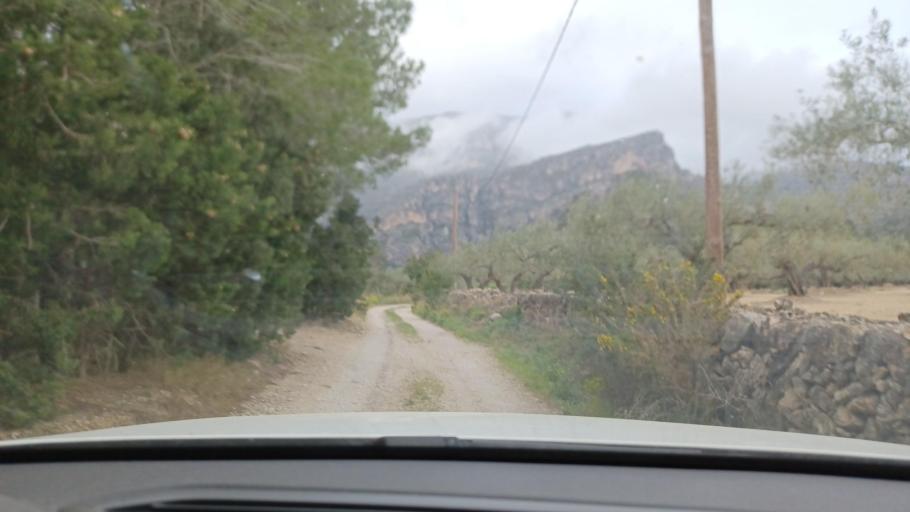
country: ES
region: Catalonia
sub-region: Provincia de Tarragona
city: Mas de Barberans
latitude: 40.8051
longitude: 0.4032
